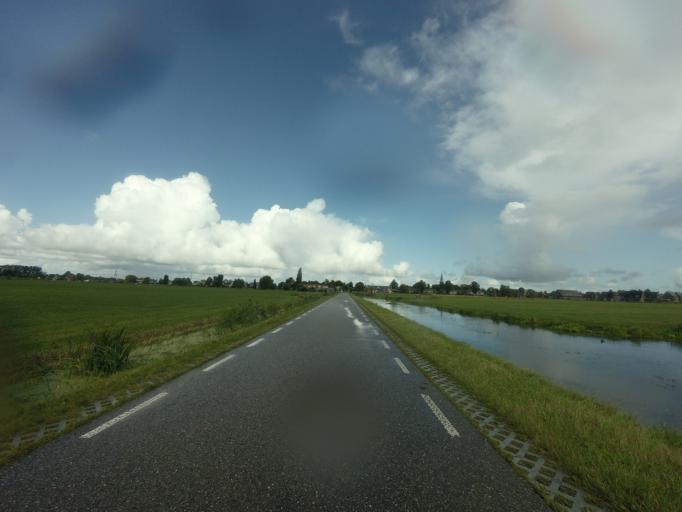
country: NL
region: Friesland
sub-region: Gemeente Leeuwarden
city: Wirdum
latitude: 53.1445
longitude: 5.8033
